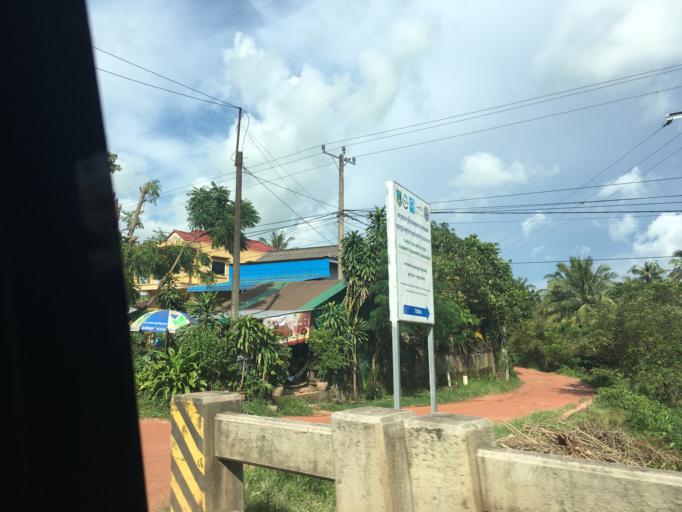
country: KH
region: Preah Sihanouk
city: Sihanoukville
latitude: 10.6292
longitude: 103.7815
